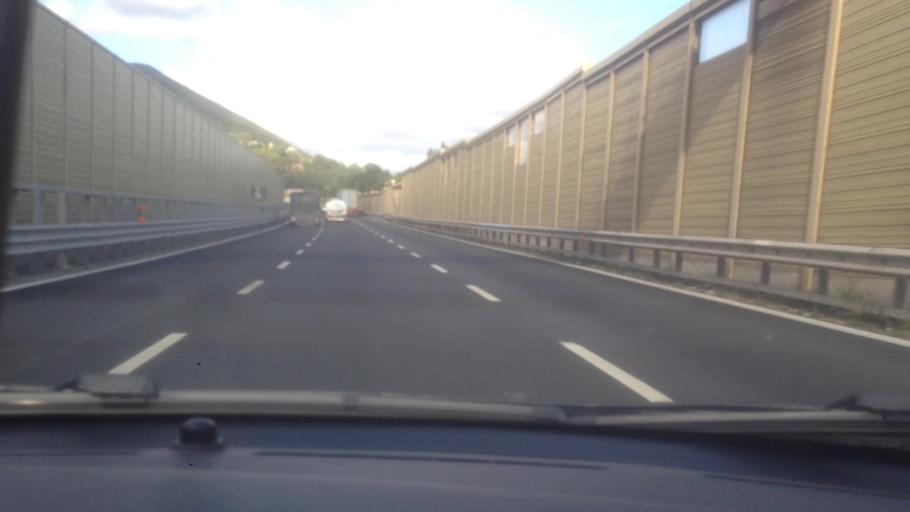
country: IT
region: Liguria
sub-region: Provincia di Genova
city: Arenzano
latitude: 44.4044
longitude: 8.6726
